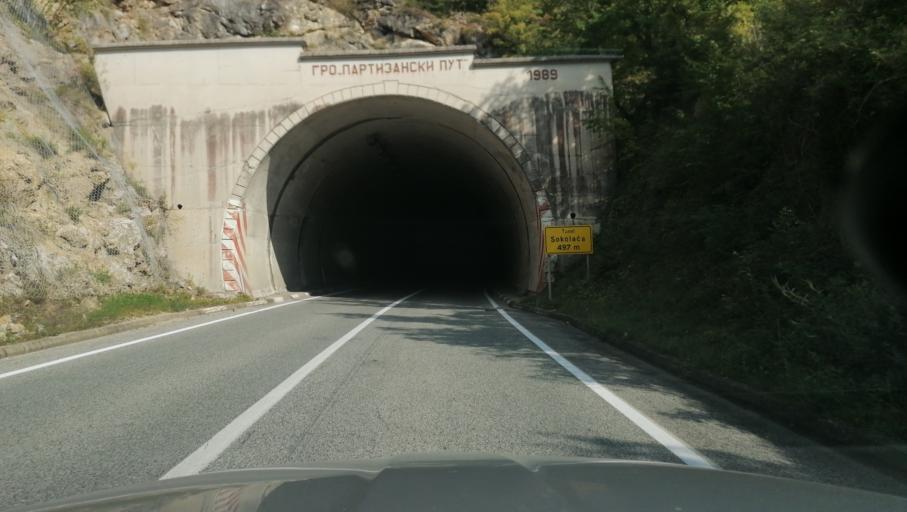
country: BA
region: Republika Srpska
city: Visegrad
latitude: 43.7540
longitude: 19.2425
